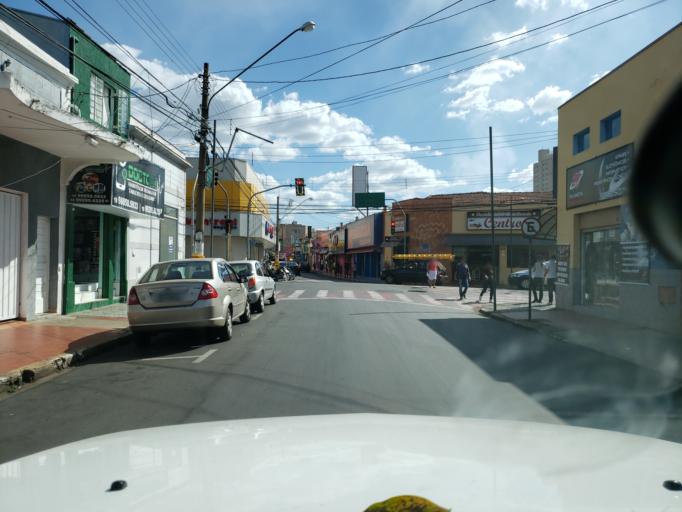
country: BR
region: Sao Paulo
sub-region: Moji-Guacu
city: Mogi-Gaucu
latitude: -22.3715
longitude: -46.9408
